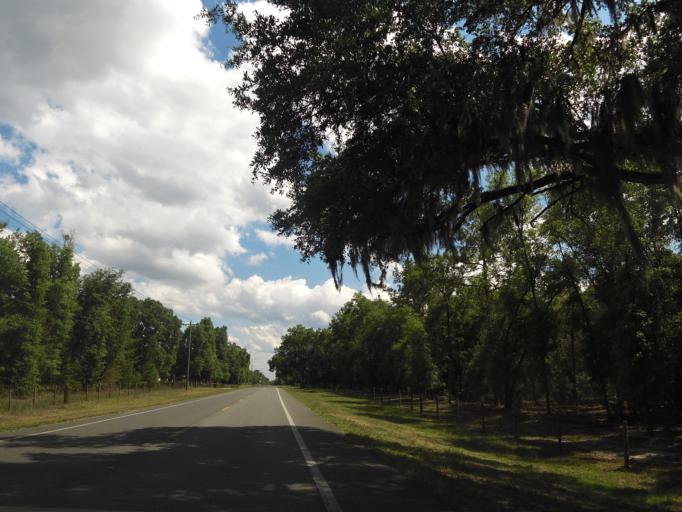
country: US
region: Florida
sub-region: Clay County
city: Keystone Heights
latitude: 29.8229
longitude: -81.9224
